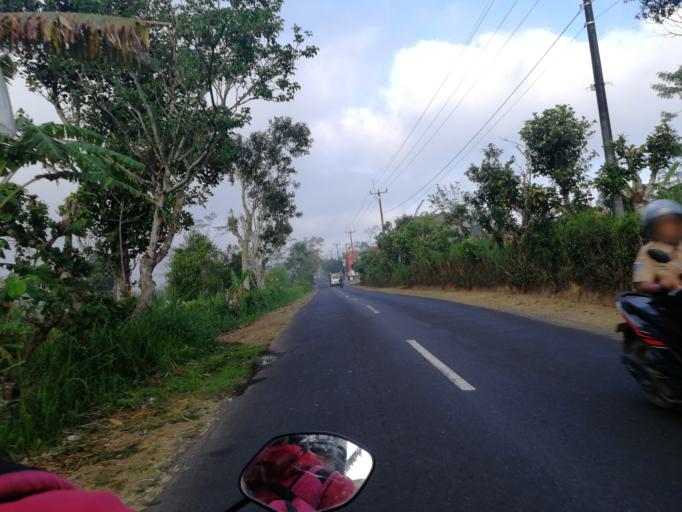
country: ID
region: Bali
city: Banjar Kedisan
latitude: -8.2238
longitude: 115.2554
